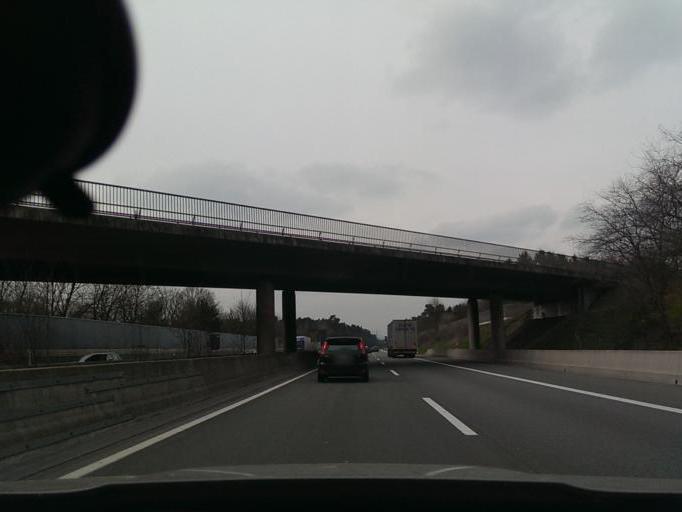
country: DE
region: North Rhine-Westphalia
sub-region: Regierungsbezirk Detmold
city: Hovelhof
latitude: 51.8778
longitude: 8.6489
